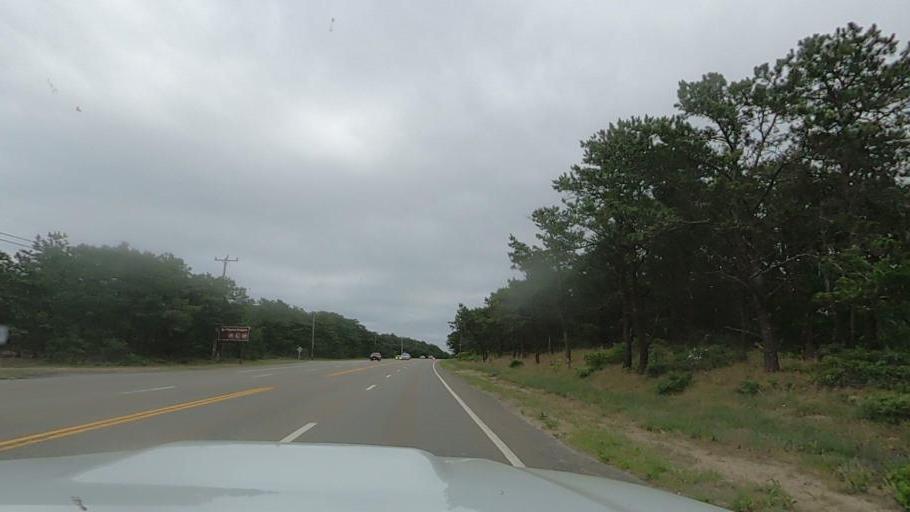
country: US
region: Massachusetts
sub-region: Barnstable County
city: Provincetown
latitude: 42.0484
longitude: -70.1061
